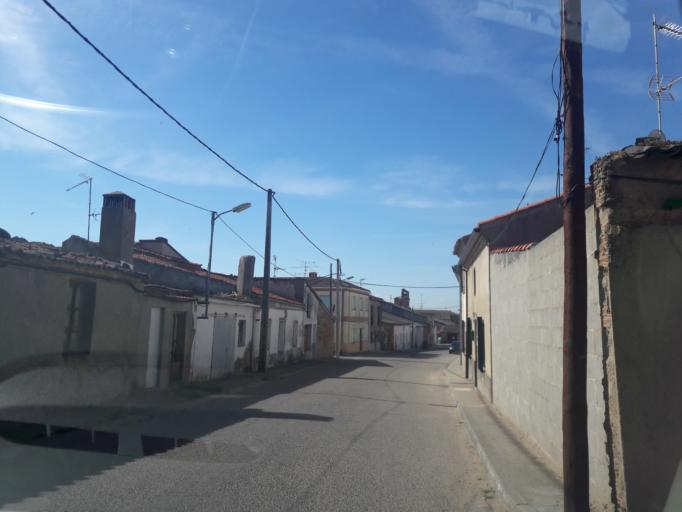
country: ES
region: Castille and Leon
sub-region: Provincia de Salamanca
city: Villoruela
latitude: 41.0102
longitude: -5.3950
